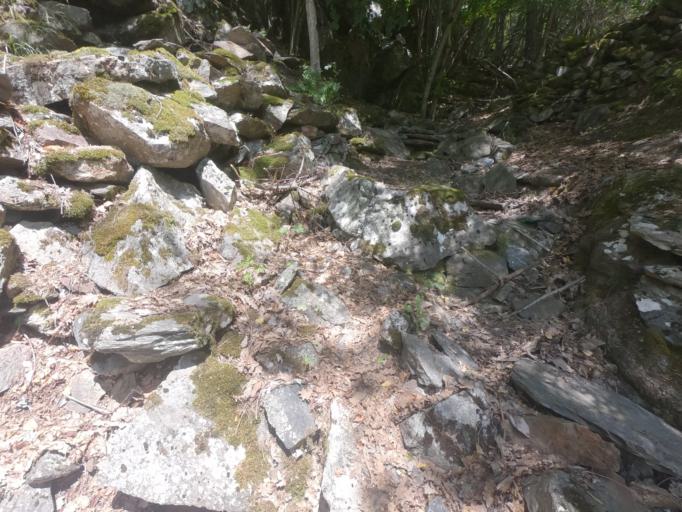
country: CH
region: Valais
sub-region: Saint-Maurice District
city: Salvan
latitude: 46.0800
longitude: 6.9781
